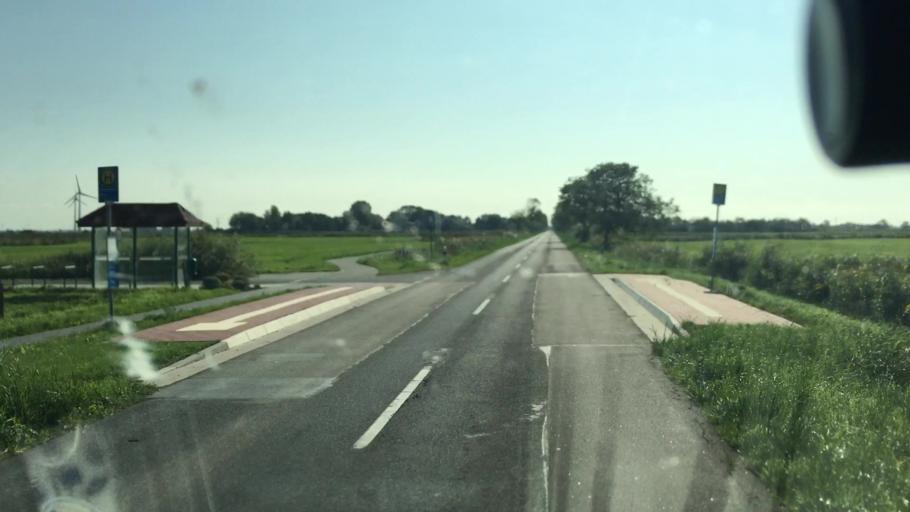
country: DE
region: Lower Saxony
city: Werdum
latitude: 53.6651
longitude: 7.6882
